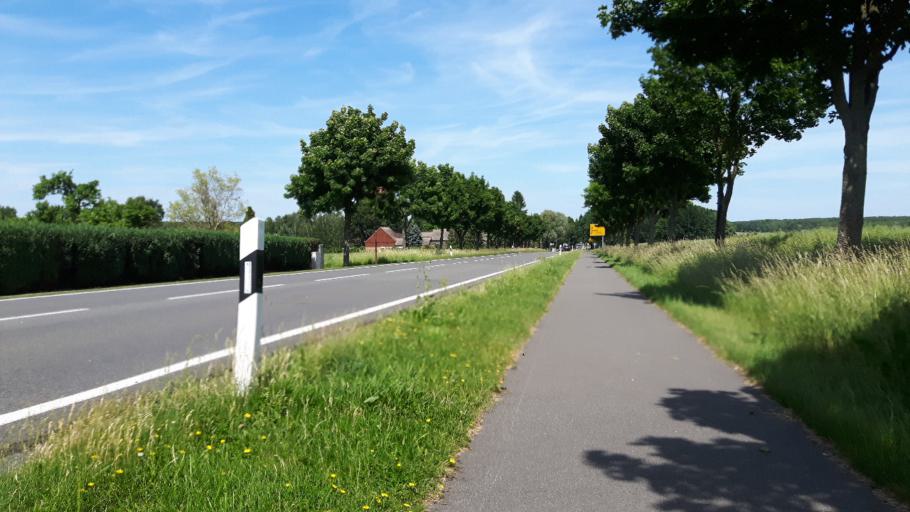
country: DE
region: Saxony-Anhalt
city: Kropstadt
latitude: 52.0246
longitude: 12.7973
